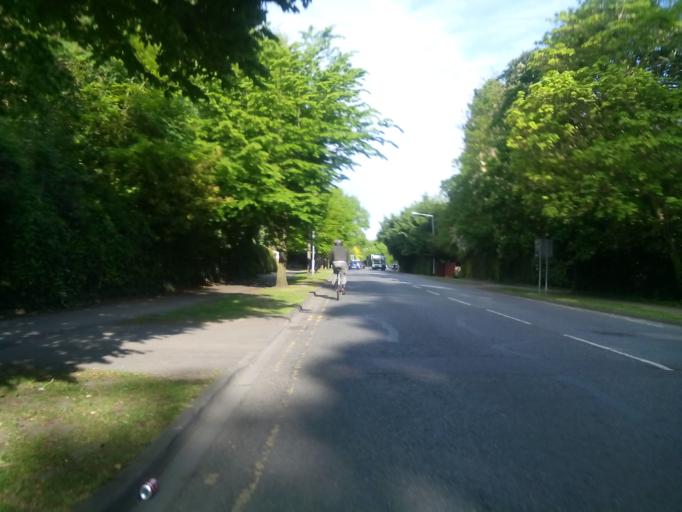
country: GB
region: England
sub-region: Cambridgeshire
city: Cambridge
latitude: 52.2108
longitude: 0.1094
